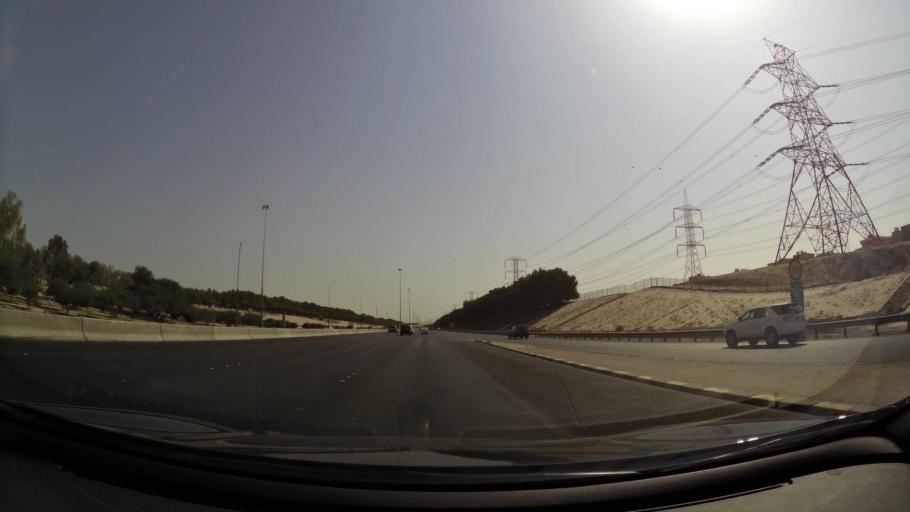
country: KW
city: Bayan
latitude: 29.3032
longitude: 48.0236
